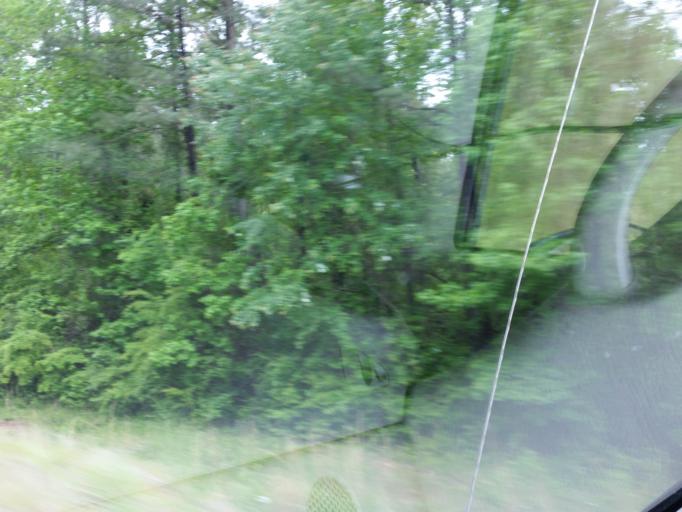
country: US
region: Georgia
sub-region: Crawford County
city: Knoxville
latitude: 32.7197
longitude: -83.9579
